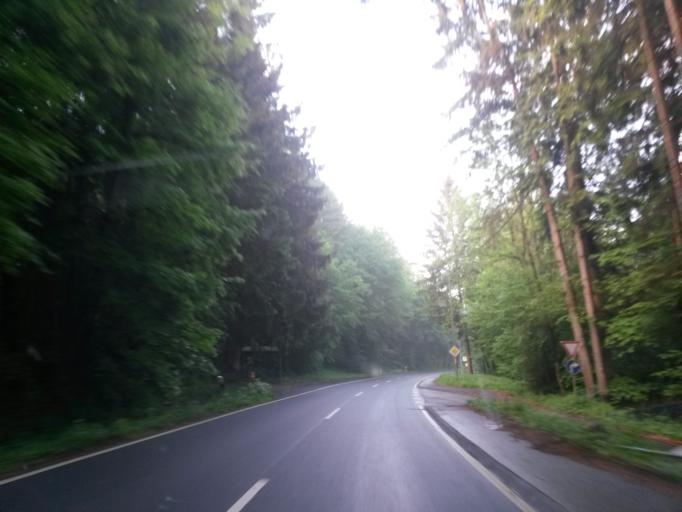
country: DE
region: North Rhine-Westphalia
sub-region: Regierungsbezirk Koln
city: Much
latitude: 50.8878
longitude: 7.4021
